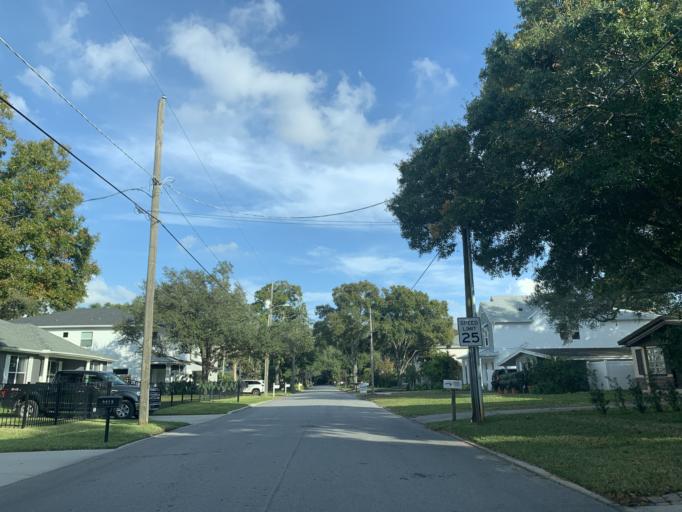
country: US
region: Florida
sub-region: Hillsborough County
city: Tampa
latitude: 27.8947
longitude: -82.5016
